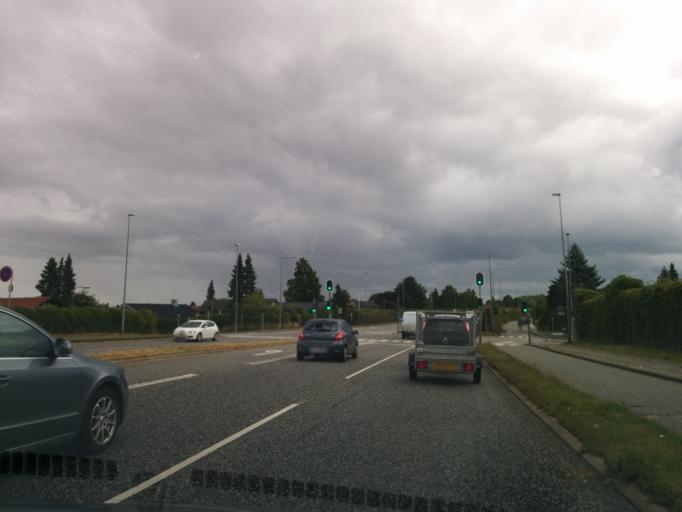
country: DK
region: Central Jutland
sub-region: Arhus Kommune
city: Arhus
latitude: 56.1721
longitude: 10.1588
